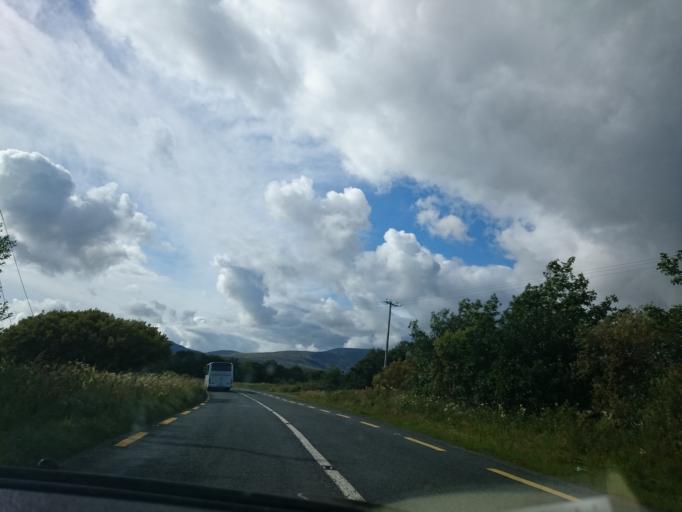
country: IE
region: Connaught
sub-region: Maigh Eo
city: Westport
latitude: 53.9025
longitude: -9.6207
